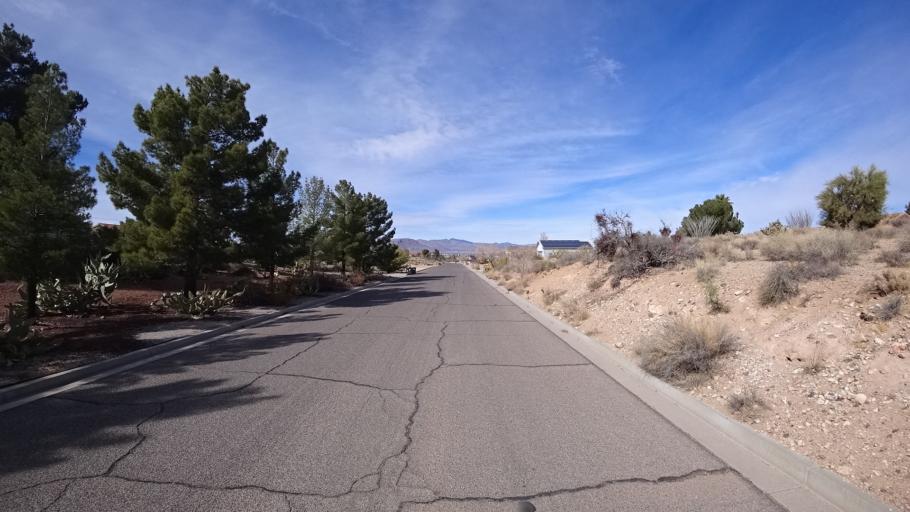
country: US
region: Arizona
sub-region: Mohave County
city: Kingman
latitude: 35.1875
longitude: -113.9885
